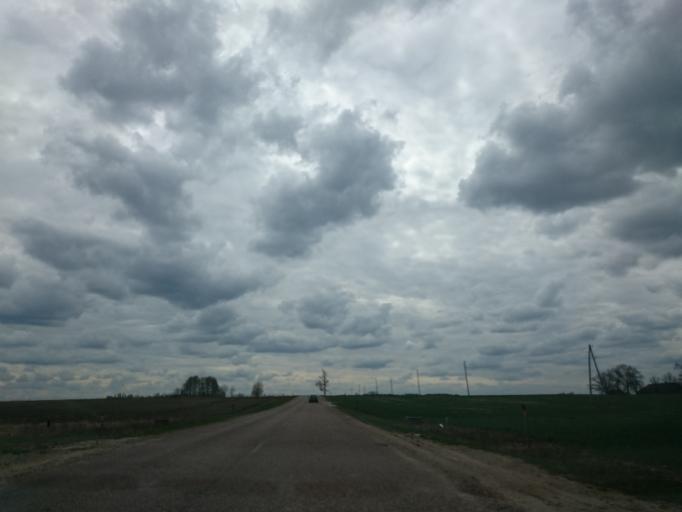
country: LV
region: Talsu Rajons
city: Sabile
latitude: 56.9540
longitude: 22.6095
